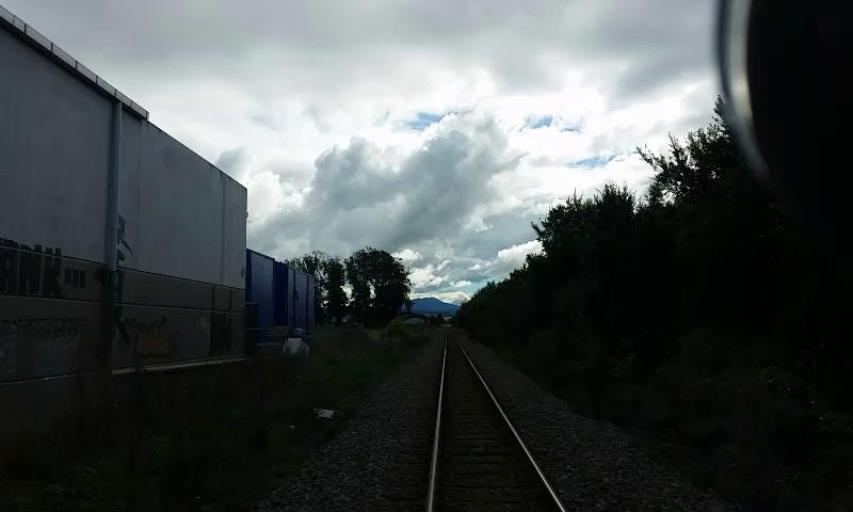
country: NZ
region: Canterbury
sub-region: Waimakariri District
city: Woodend
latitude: -43.3167
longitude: 172.6016
